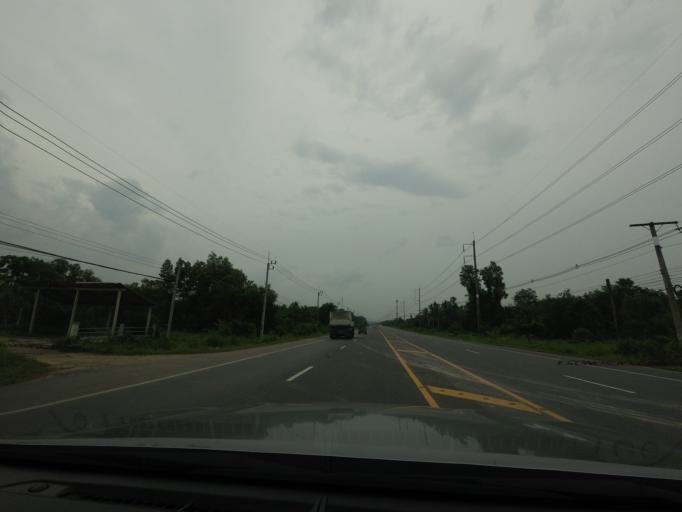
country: TH
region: Songkhla
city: Na Mom
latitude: 7.0325
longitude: 100.6614
